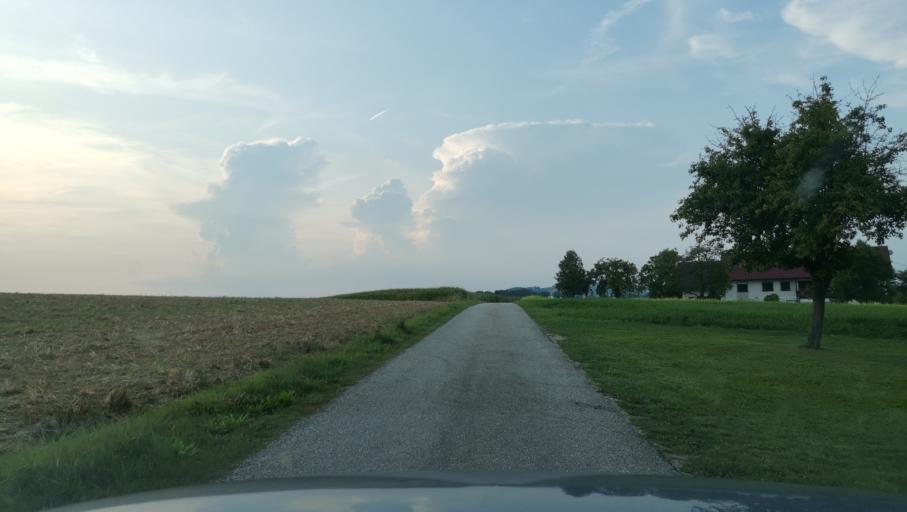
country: AT
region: Upper Austria
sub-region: Politischer Bezirk Grieskirchen
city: Grieskirchen
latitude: 48.3069
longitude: 13.8090
